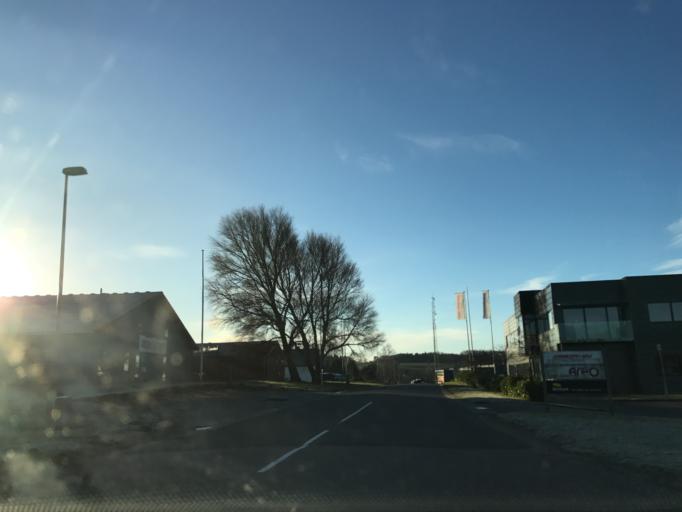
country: DK
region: Central Jutland
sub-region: Silkeborg Kommune
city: Svejbaek
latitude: 56.1583
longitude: 9.6467
